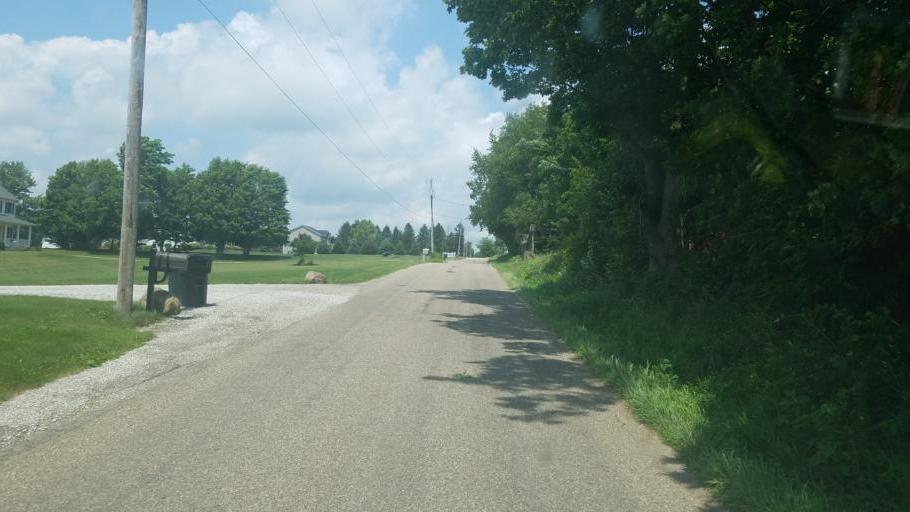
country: US
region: Ohio
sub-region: Richland County
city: Lexington
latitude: 40.6508
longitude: -82.6018
